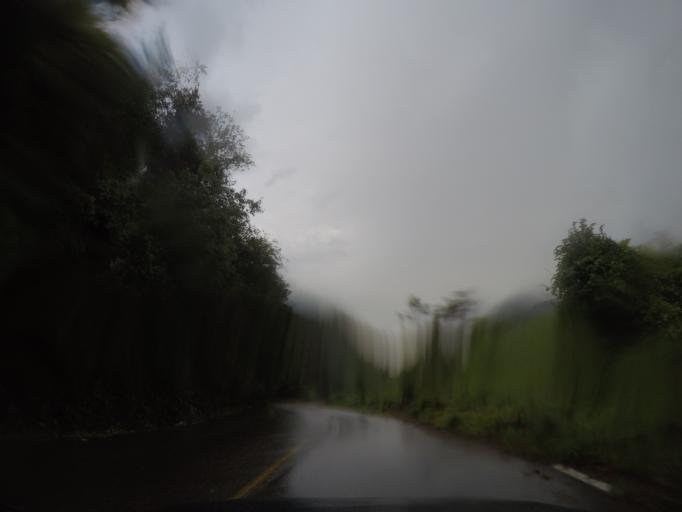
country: MX
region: Oaxaca
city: San Gabriel Mixtepec
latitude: 16.0696
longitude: -97.0767
